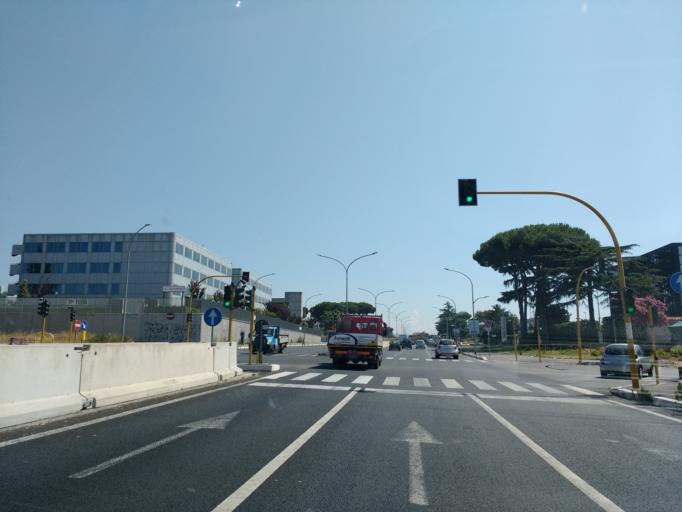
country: IT
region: Latium
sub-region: Citta metropolitana di Roma Capitale
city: Setteville
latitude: 41.9358
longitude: 12.6122
